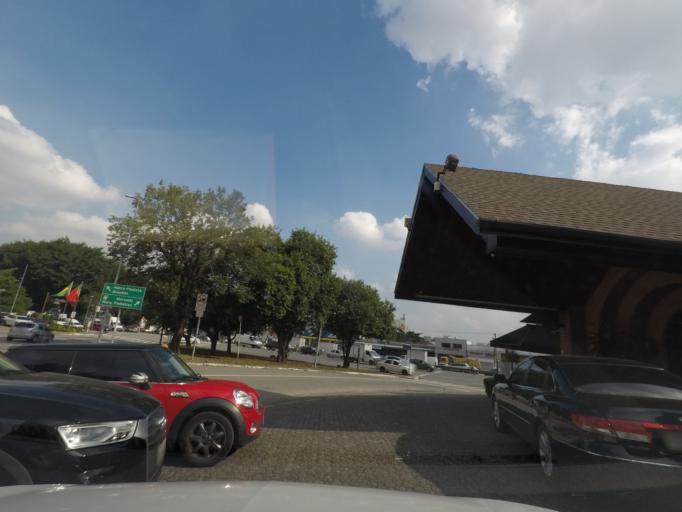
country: BR
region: Sao Paulo
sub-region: Sao Paulo
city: Sao Paulo
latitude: -23.6085
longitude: -46.6784
